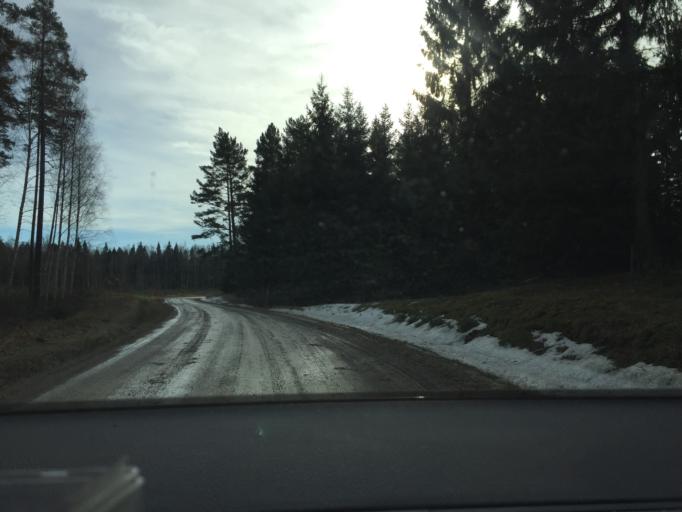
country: SE
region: OErebro
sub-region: Orebro Kommun
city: Odensbacken
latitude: 59.1217
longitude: 15.4720
